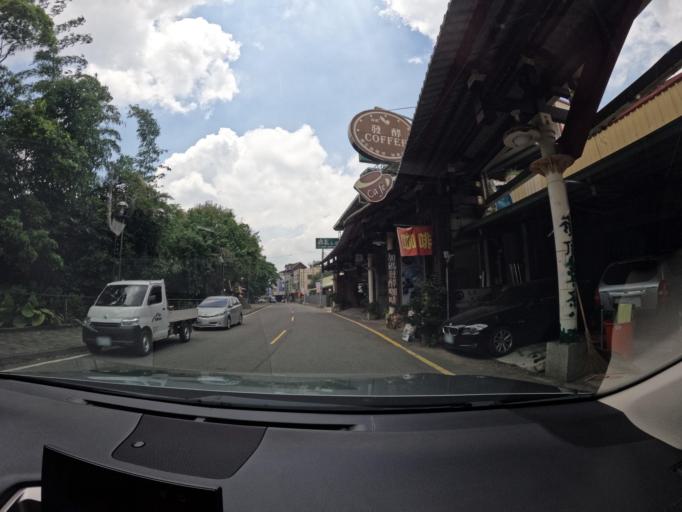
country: TW
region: Taiwan
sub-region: Nantou
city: Nantou
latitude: 23.8333
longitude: 120.6359
